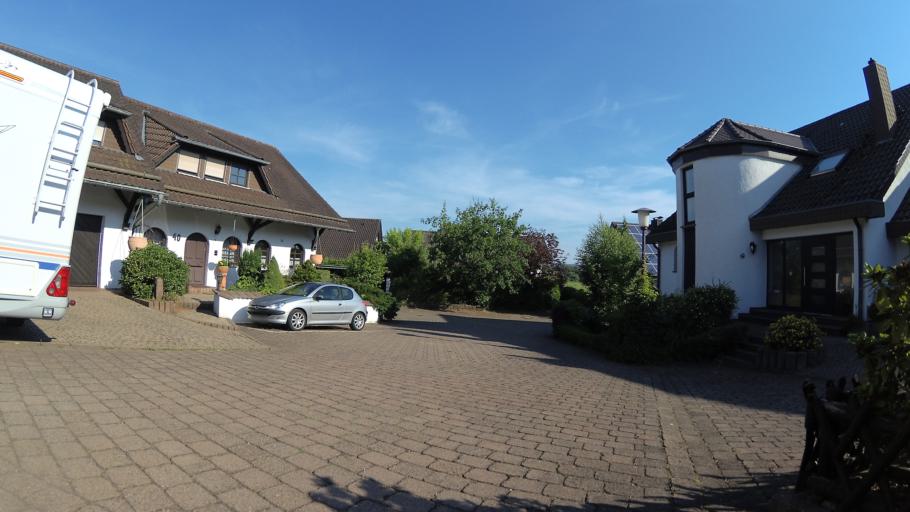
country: DE
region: Saarland
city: Homburg
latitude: 49.3424
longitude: 7.3220
